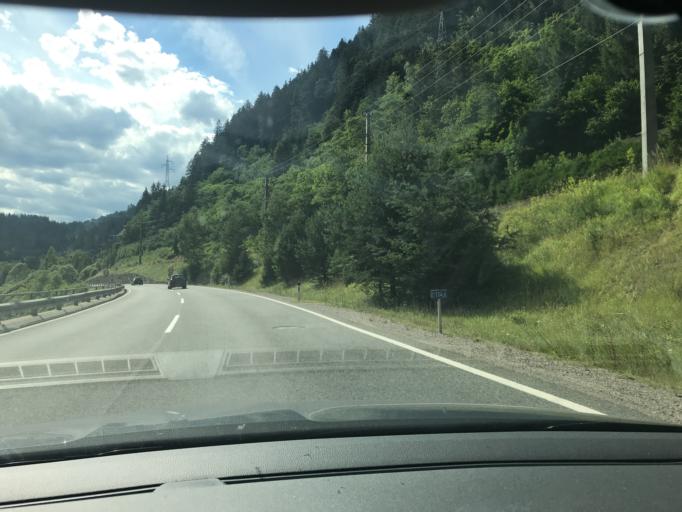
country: AT
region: Tyrol
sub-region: Politischer Bezirk Lienz
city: Leisach
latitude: 46.7918
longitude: 12.7144
